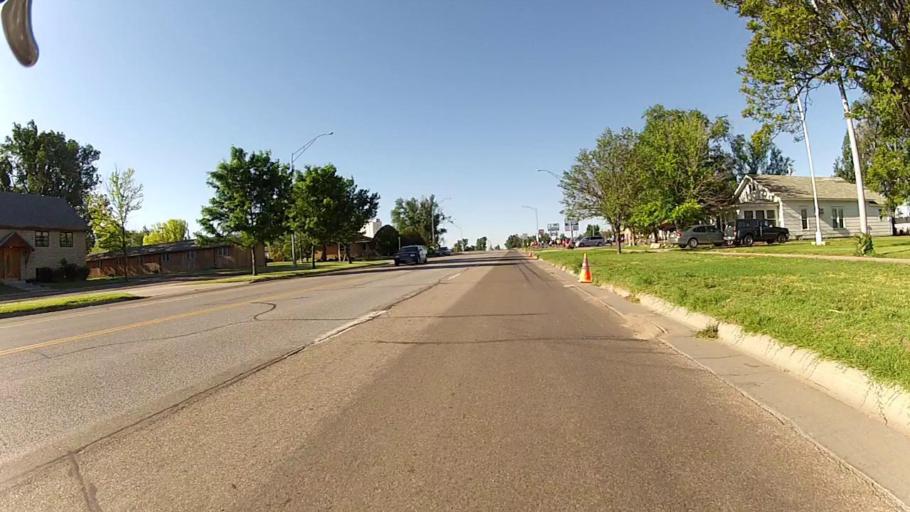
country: US
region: Kansas
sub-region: Ford County
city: Dodge City
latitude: 37.6372
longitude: -99.7539
